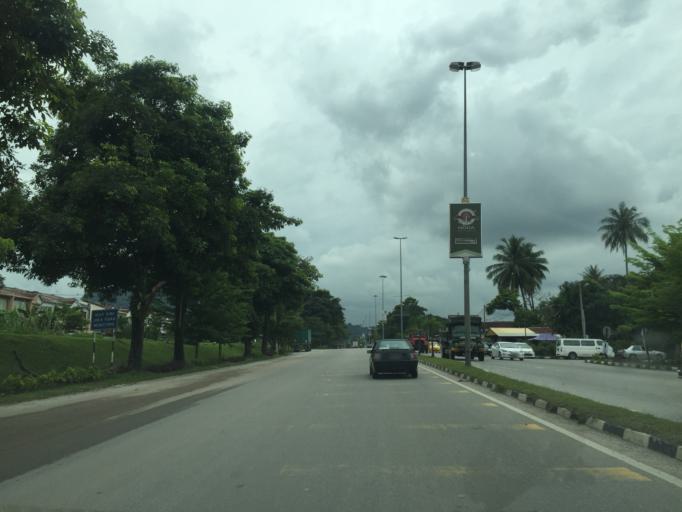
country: MY
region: Perak
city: Ipoh
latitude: 4.5404
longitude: 101.1233
